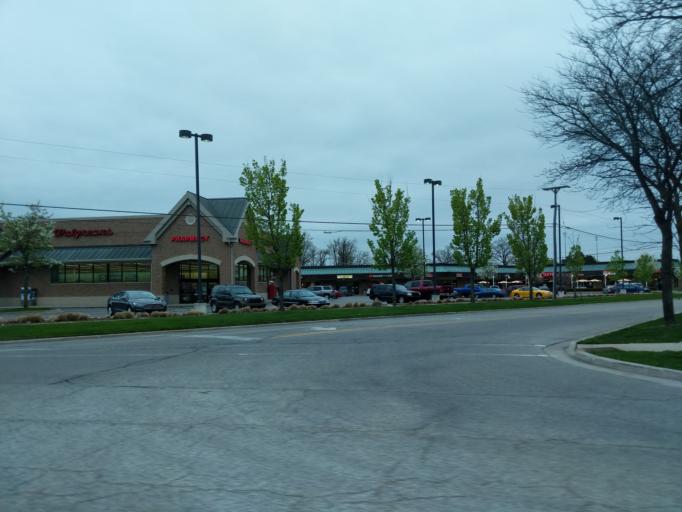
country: US
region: Michigan
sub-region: Midland County
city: Midland
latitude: 43.6192
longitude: -84.2192
